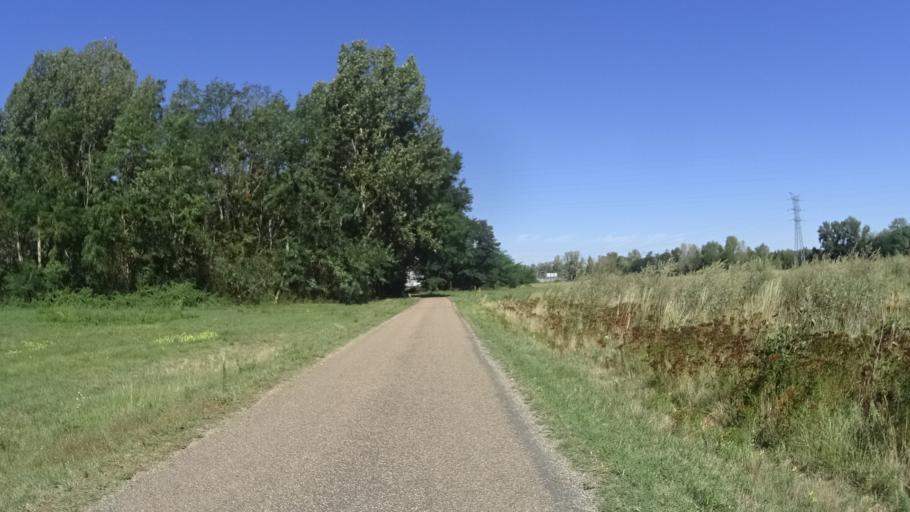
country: FR
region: Bourgogne
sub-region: Departement de la Nievre
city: Neuvy-sur-Loire
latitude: 47.4986
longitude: 2.8858
